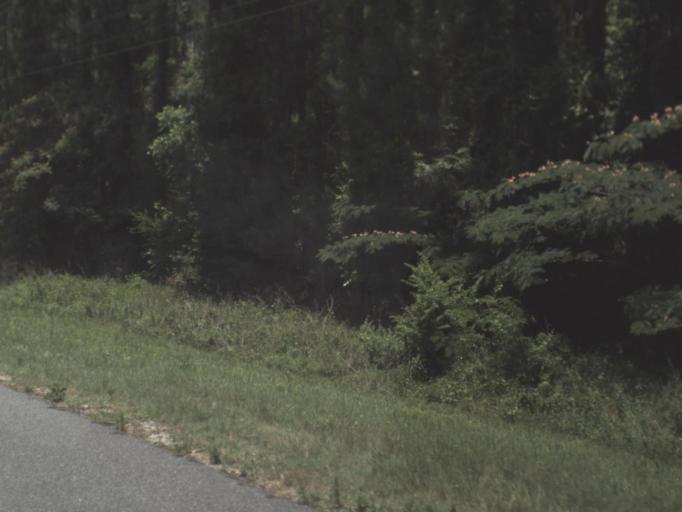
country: US
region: Florida
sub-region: Lafayette County
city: Mayo
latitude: 29.9466
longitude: -82.9488
